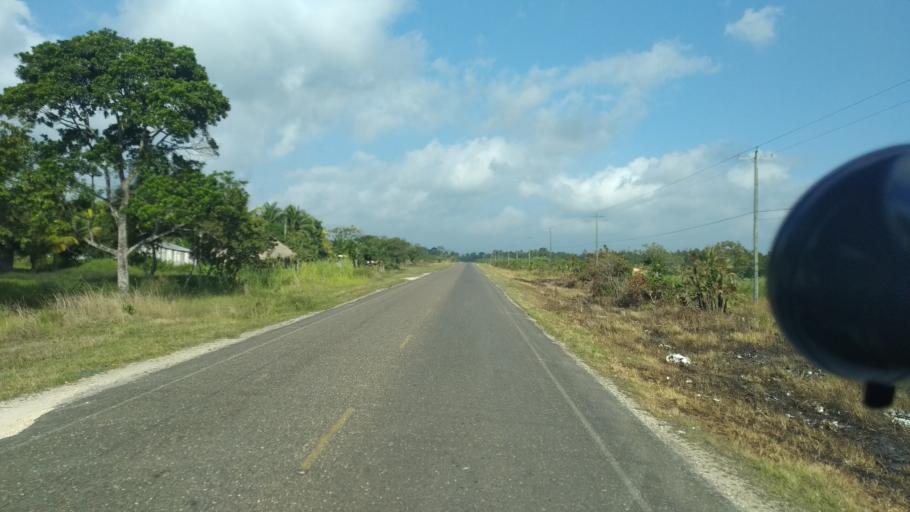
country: BZ
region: Stann Creek
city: Placencia
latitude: 16.5142
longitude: -88.5453
